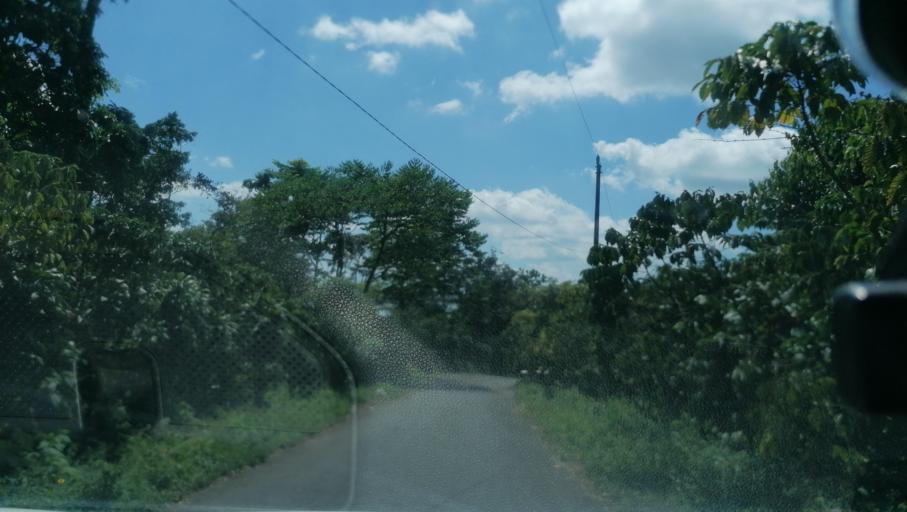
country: MX
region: Chiapas
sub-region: Cacahoatan
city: Benito Juarez
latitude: 15.0597
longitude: -92.1460
